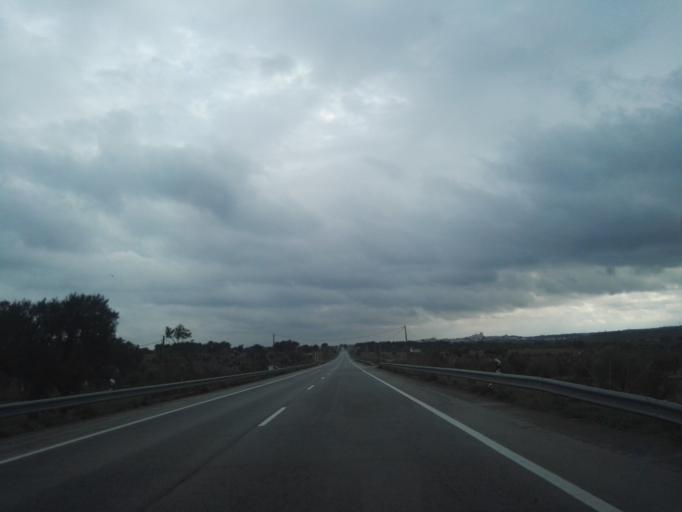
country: PT
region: Portalegre
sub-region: Arronches
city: Arronches
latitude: 39.1415
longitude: -7.2993
